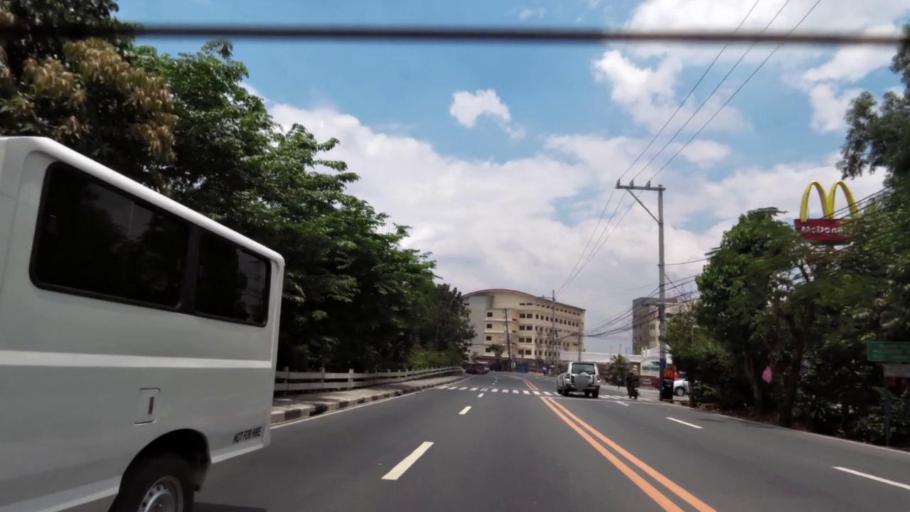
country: PH
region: Calabarzon
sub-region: Province of Rizal
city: Antipolo
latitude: 14.6178
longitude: 121.1525
